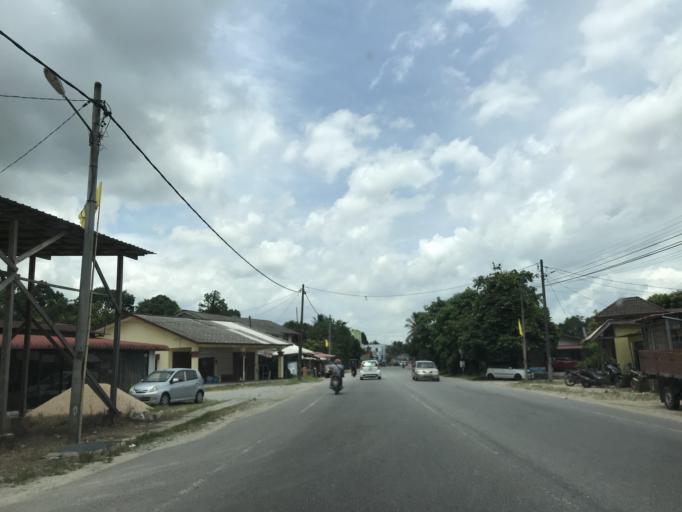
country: MY
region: Kelantan
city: Kota Bharu
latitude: 6.0787
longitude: 102.2083
